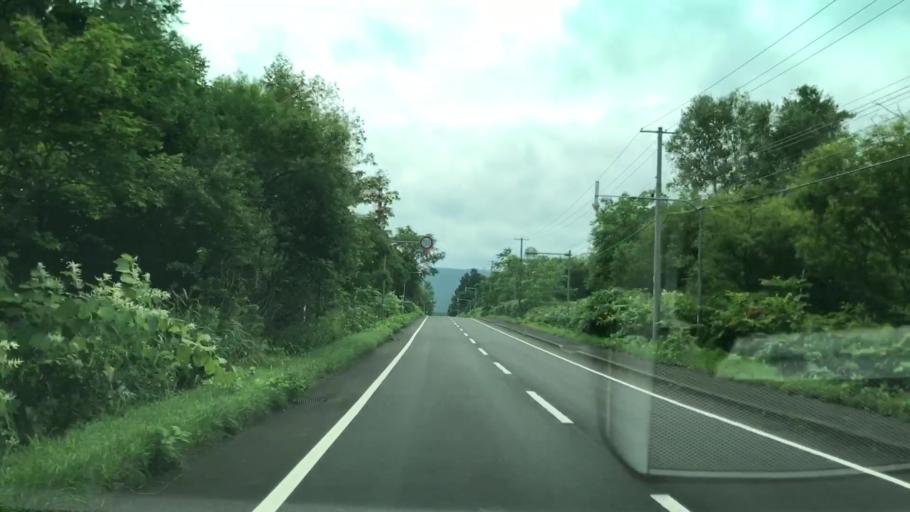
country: JP
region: Hokkaido
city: Yoichi
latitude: 43.0693
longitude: 140.8185
